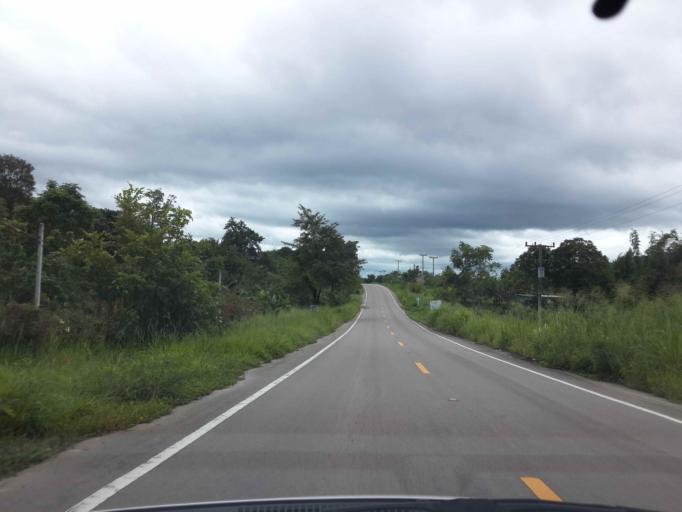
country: TH
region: Ratchaburi
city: Suan Phueng
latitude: 13.6788
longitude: 99.2002
